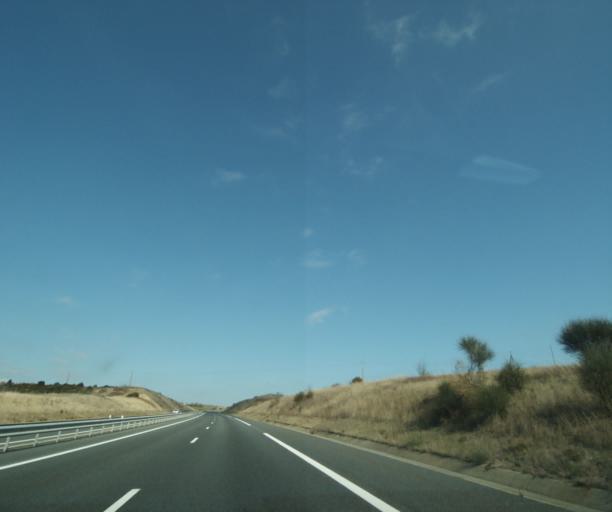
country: FR
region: Midi-Pyrenees
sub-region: Departement de l'Aveyron
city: Creissels
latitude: 44.1126
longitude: 3.0298
